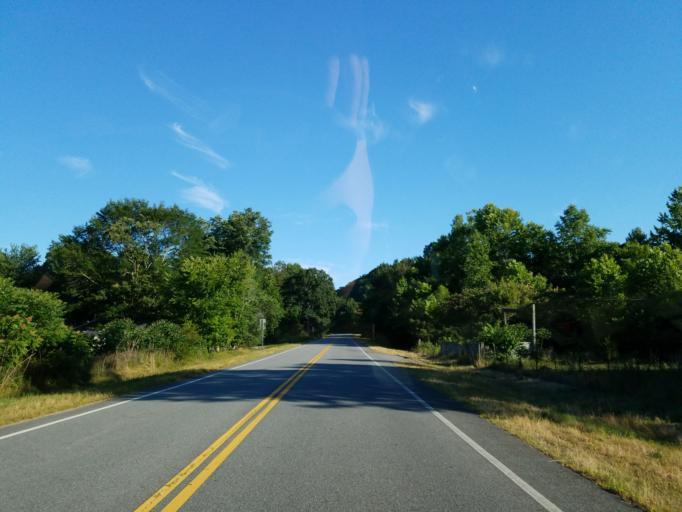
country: US
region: Georgia
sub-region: Gordon County
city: Calhoun
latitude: 34.6068
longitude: -85.0448
